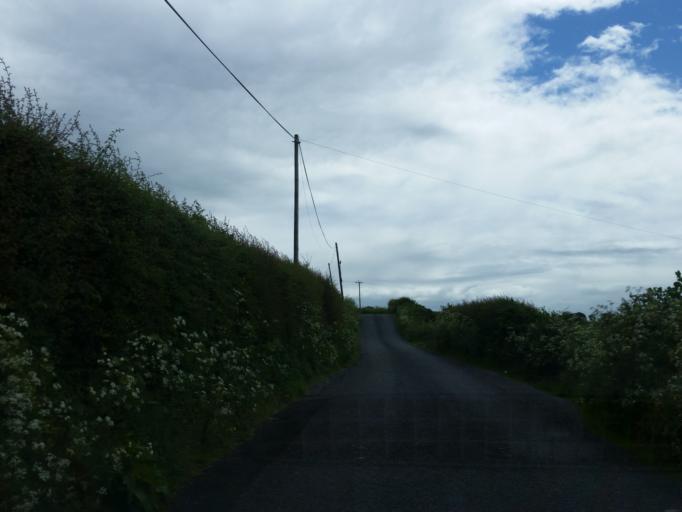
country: GB
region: Northern Ireland
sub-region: Omagh District
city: Omagh
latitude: 54.5329
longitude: -7.1403
